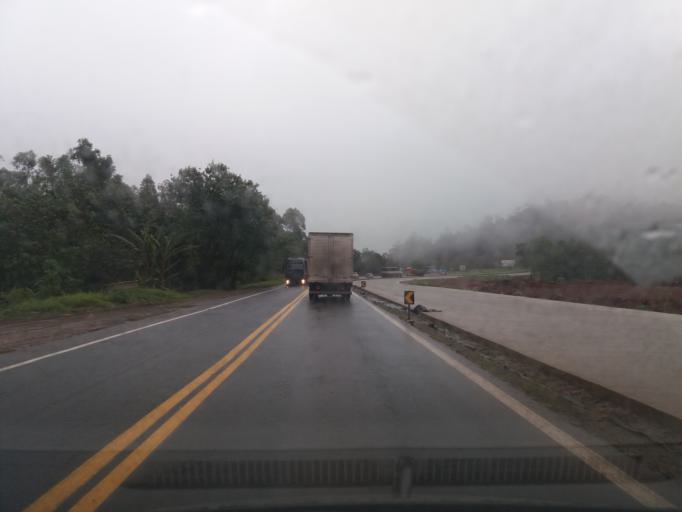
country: BR
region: Parana
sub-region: Realeza
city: Realeza
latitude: -25.4598
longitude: -53.5830
